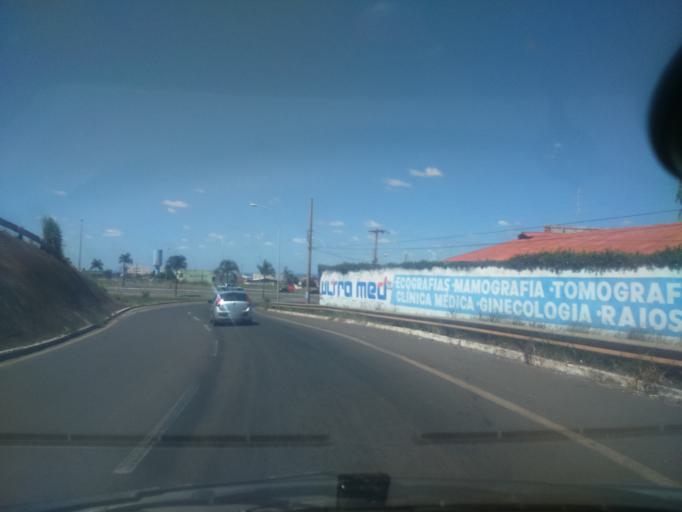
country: BR
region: Goias
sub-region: Luziania
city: Luziania
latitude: -16.0499
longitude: -47.9825
